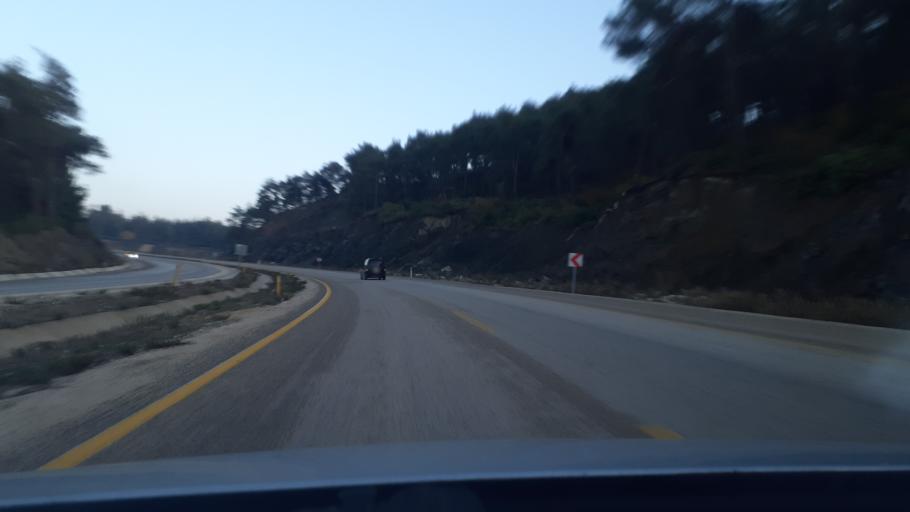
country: TR
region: Hatay
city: Yayladagi
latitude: 35.8908
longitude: 36.0878
